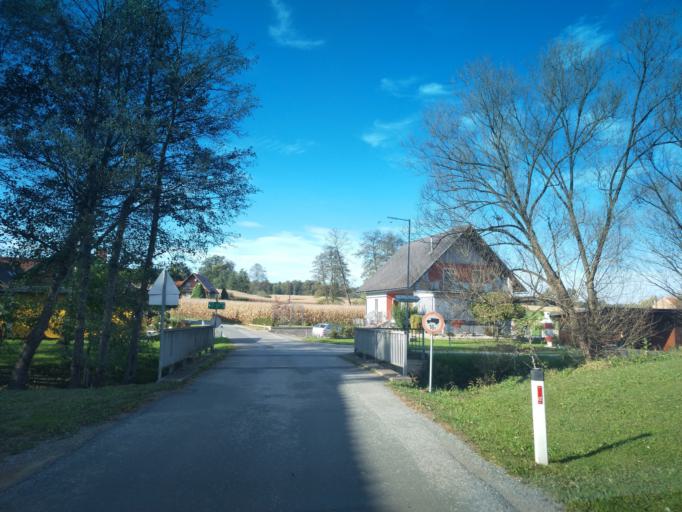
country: AT
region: Styria
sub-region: Politischer Bezirk Leibnitz
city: Sankt Johann im Saggautal
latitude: 46.7005
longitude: 15.3876
